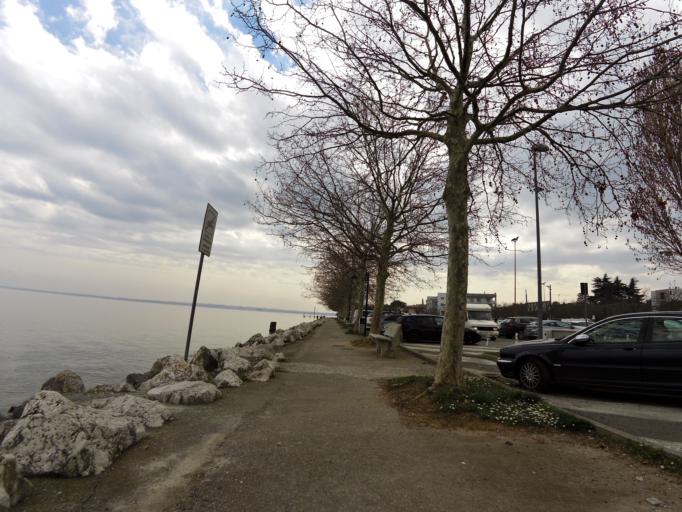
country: IT
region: Lombardy
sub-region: Provincia di Brescia
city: Sirmione
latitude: 45.4878
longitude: 10.6106
